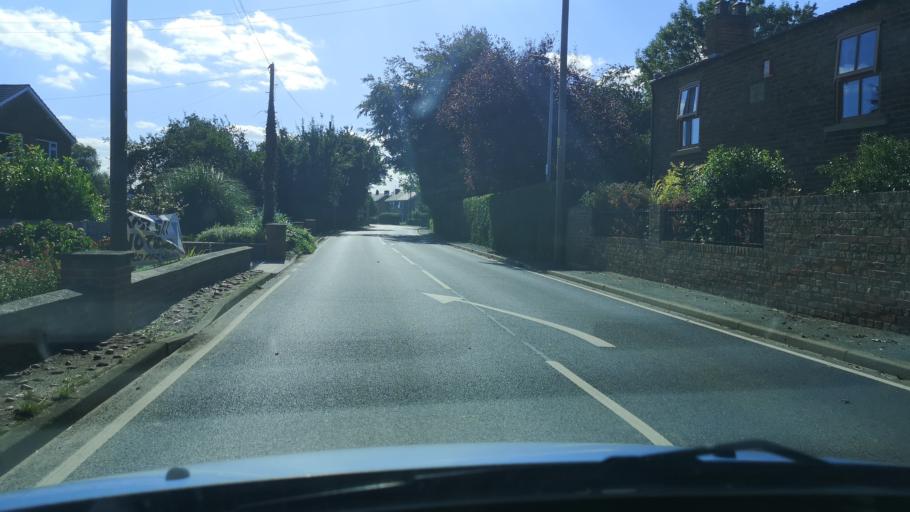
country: GB
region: England
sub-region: North Lincolnshire
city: Eastoft
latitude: 53.6350
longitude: -0.7879
